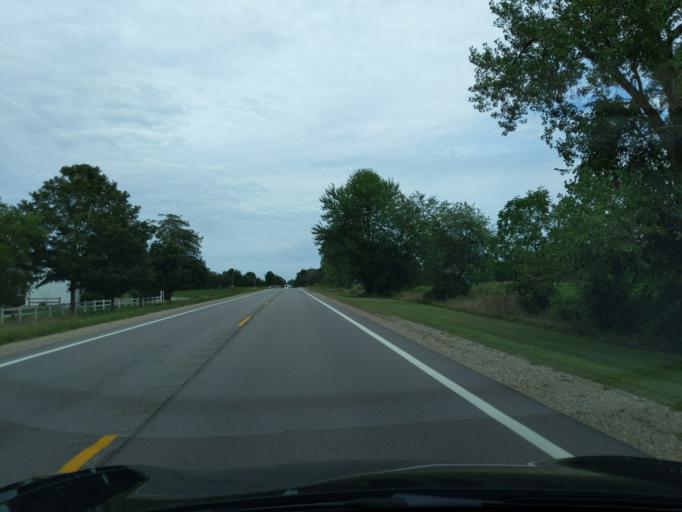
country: US
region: Michigan
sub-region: Barry County
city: Nashville
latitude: 42.5673
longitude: -85.0668
